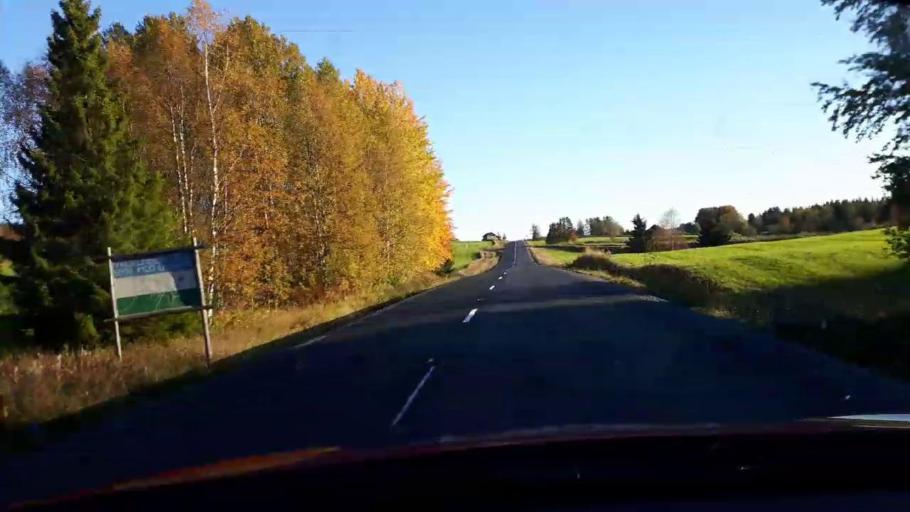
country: SE
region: Jaemtland
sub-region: OEstersunds Kommun
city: Lit
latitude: 63.4466
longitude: 14.8375
